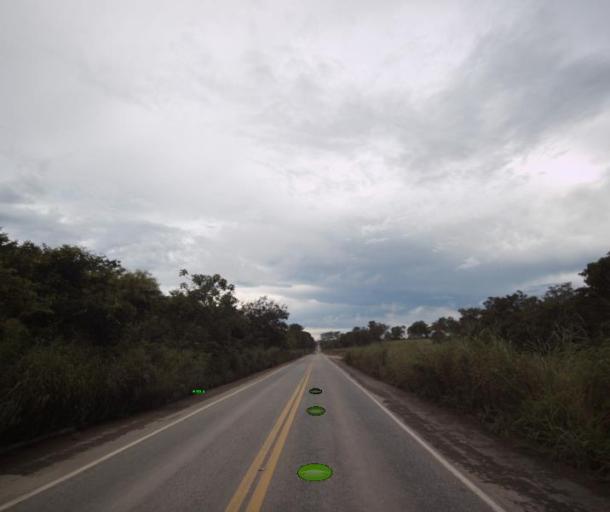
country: BR
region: Goias
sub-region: Porangatu
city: Porangatu
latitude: -13.5523
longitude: -49.0903
